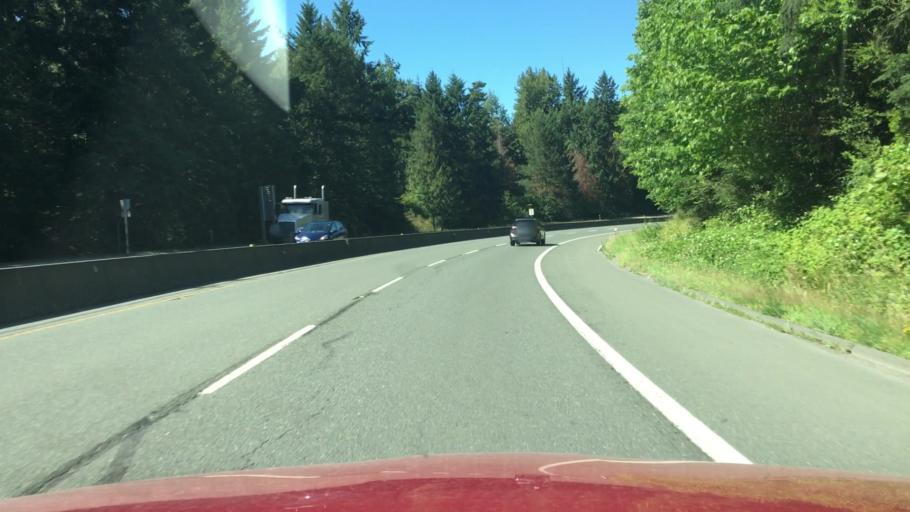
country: CA
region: British Columbia
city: North Saanich
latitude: 48.6729
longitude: -123.4287
